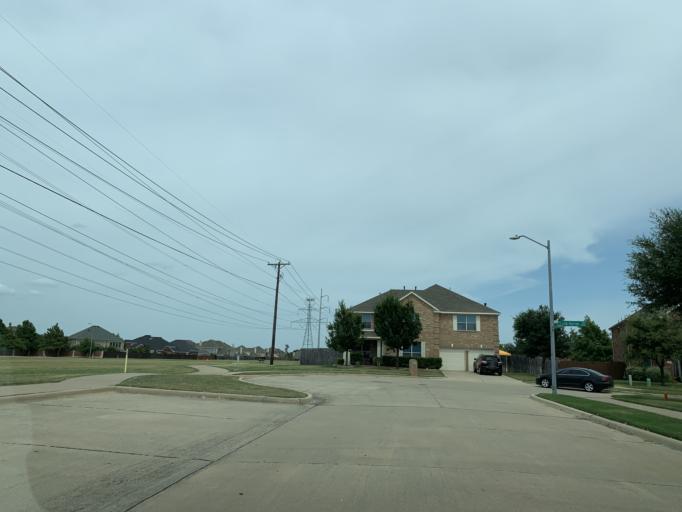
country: US
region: Texas
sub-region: Dallas County
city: Grand Prairie
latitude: 32.6539
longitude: -97.0405
